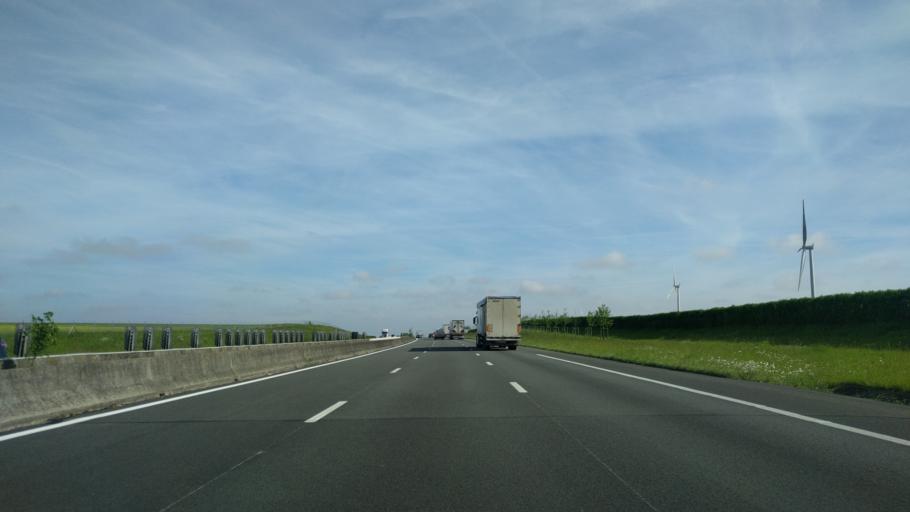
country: FR
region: Nord-Pas-de-Calais
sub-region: Departement du Pas-de-Calais
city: Bapaume
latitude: 50.0301
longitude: 2.8845
